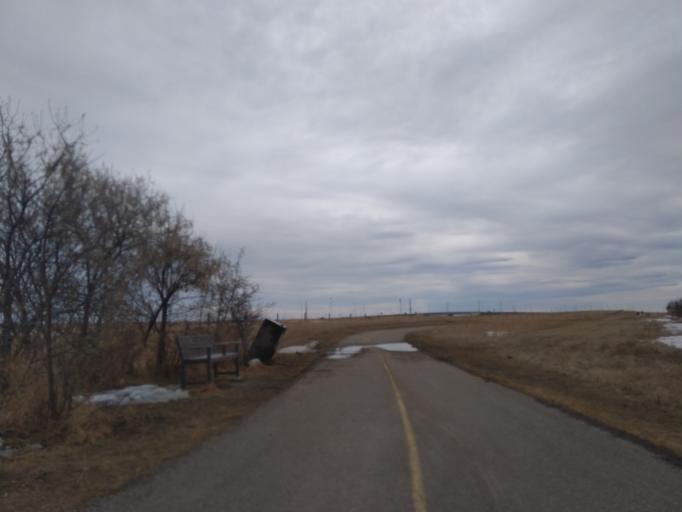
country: CA
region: Alberta
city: Chestermere
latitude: 51.1046
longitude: -113.9228
